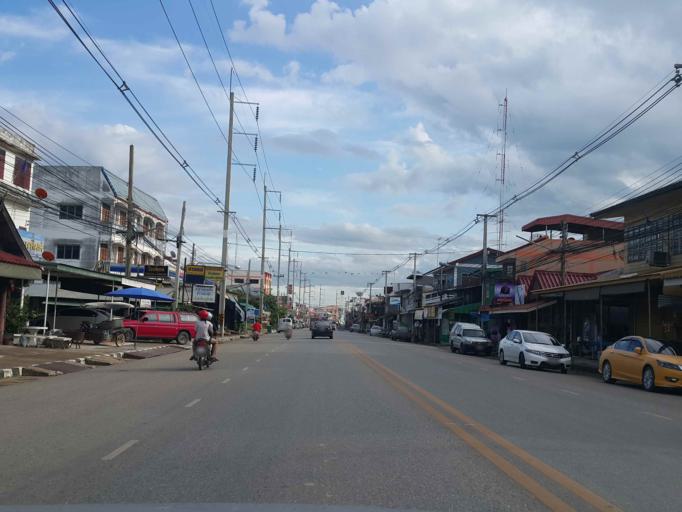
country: TH
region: Sukhothai
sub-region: Amphoe Si Satchanalai
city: Si Satchanalai
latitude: 17.5228
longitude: 99.7652
